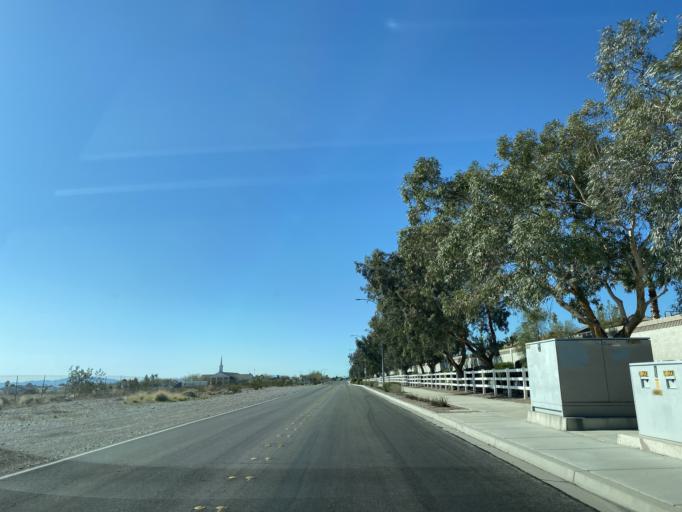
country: US
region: Nevada
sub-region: Clark County
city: North Las Vegas
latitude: 36.3246
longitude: -115.2877
